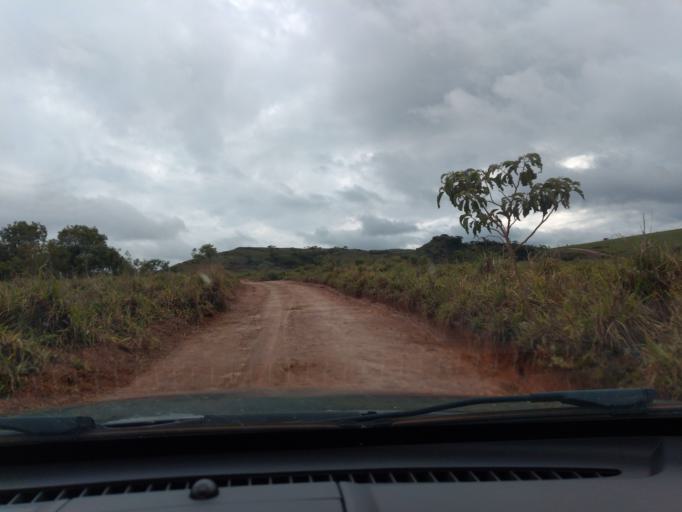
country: BR
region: Minas Gerais
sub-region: Lavras
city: Lavras
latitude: -21.5140
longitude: -44.9292
